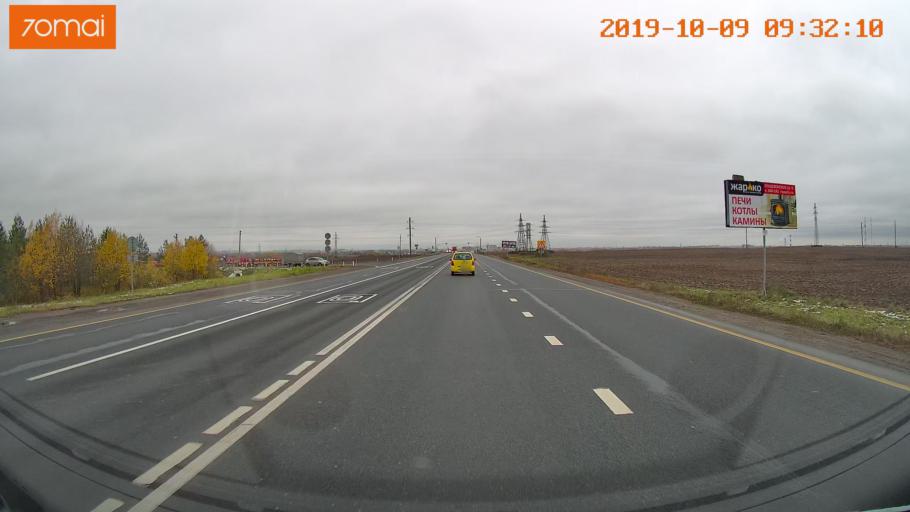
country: RU
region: Vologda
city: Vologda
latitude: 59.1561
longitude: 39.9314
